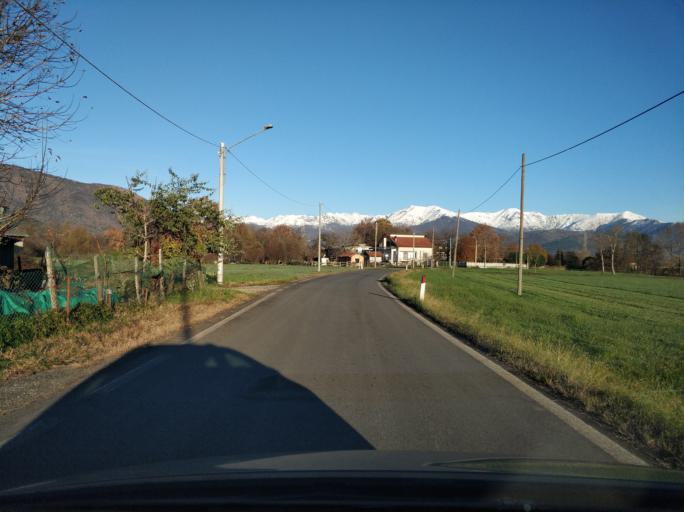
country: IT
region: Piedmont
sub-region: Provincia di Torino
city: Fiano
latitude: 45.2274
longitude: 7.5404
